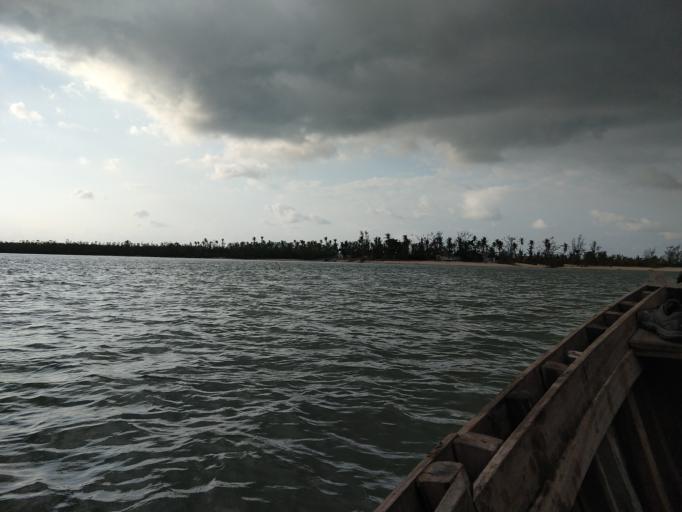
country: MZ
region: Sofala
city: Beira
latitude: -19.6801
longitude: 35.1359
